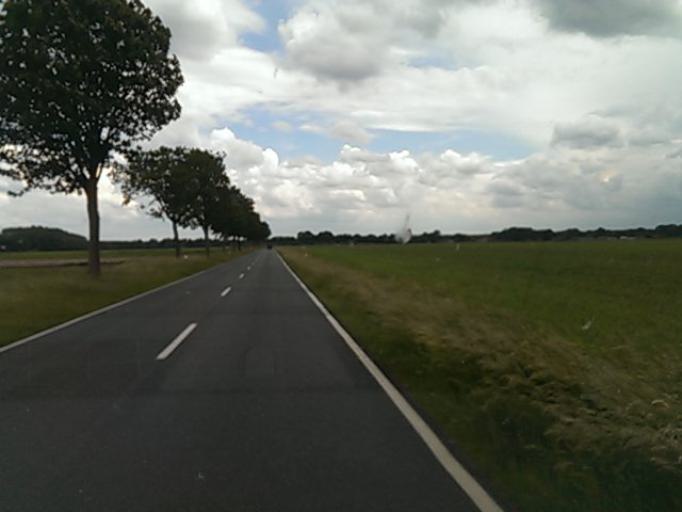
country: DE
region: Lower Saxony
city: Hermannsburg
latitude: 52.8061
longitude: 10.0717
